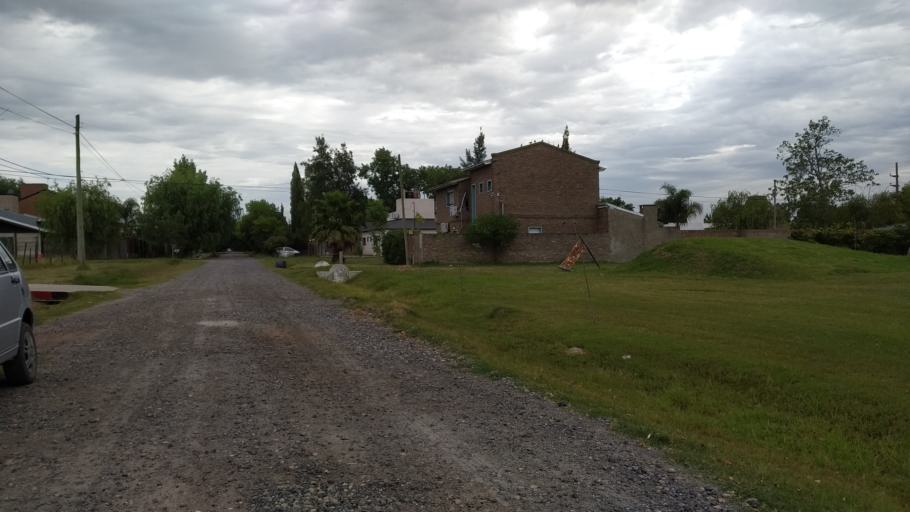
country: AR
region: Santa Fe
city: Funes
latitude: -32.9307
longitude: -60.8015
